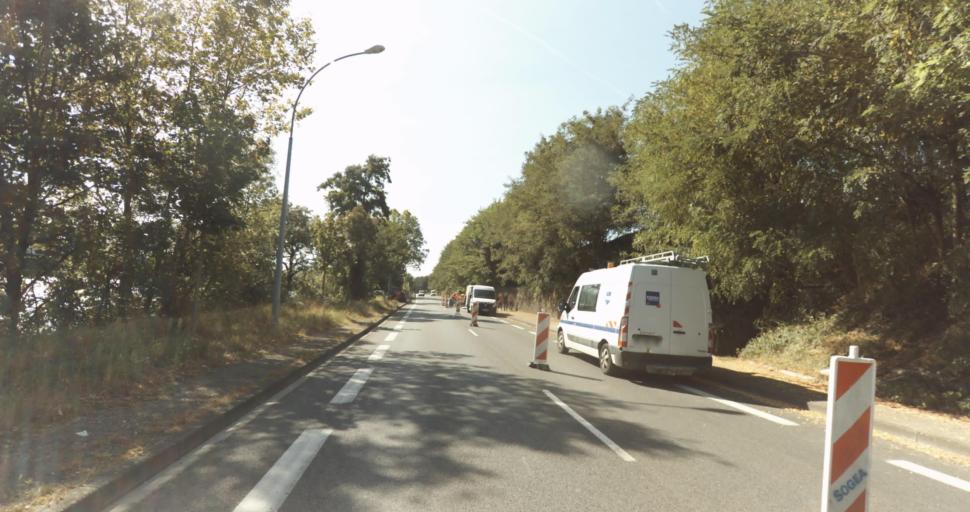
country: FR
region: Rhone-Alpes
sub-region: Departement du Rhone
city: Albigny-sur-Saone
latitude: 45.8689
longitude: 4.8346
